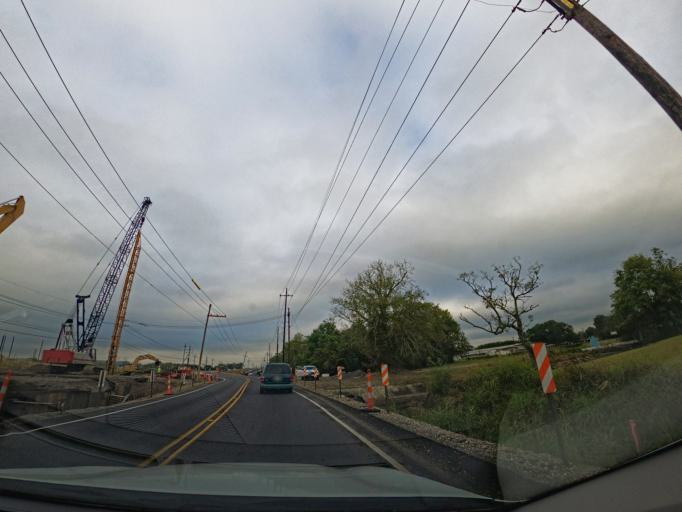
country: US
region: Louisiana
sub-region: Terrebonne Parish
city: Houma
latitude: 29.5725
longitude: -90.6956
